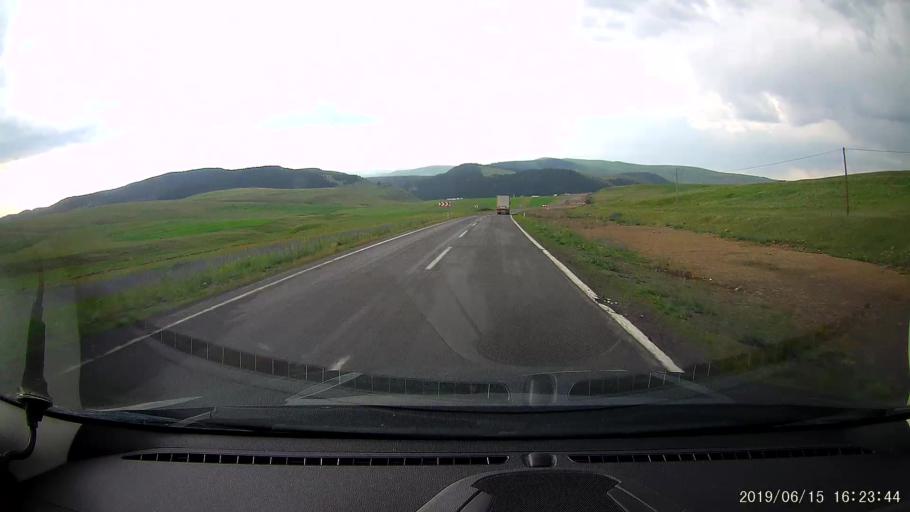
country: TR
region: Ardahan
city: Hanak
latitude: 41.1743
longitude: 42.8651
